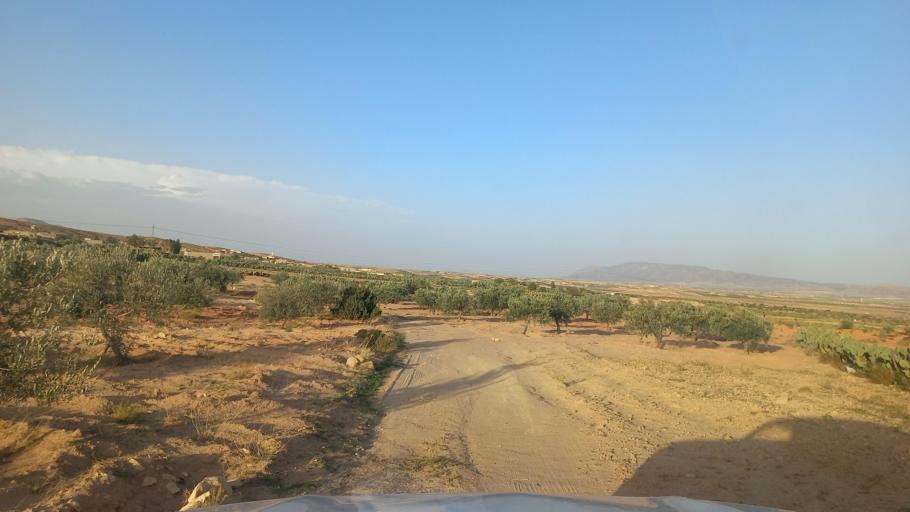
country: TN
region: Al Qasrayn
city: Sbiba
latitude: 35.3716
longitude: 9.0059
